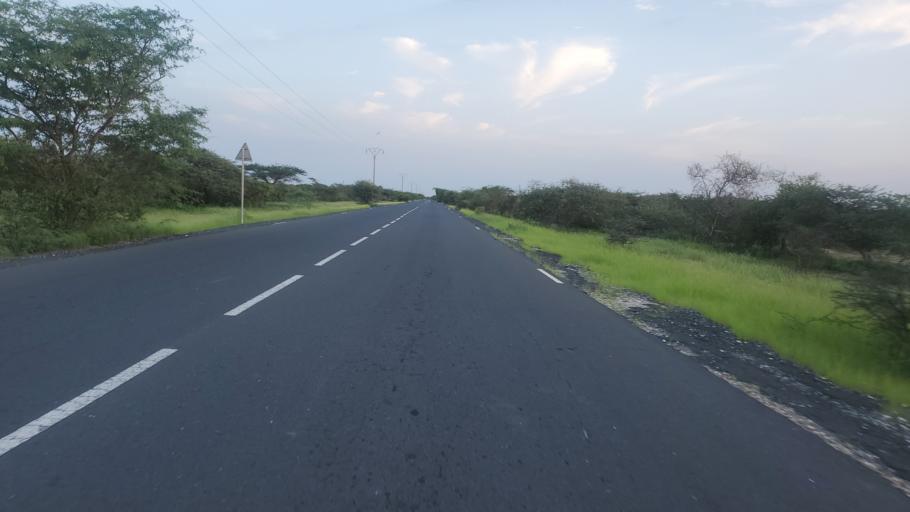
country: SN
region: Saint-Louis
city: Saint-Louis
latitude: 16.1169
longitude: -16.4137
